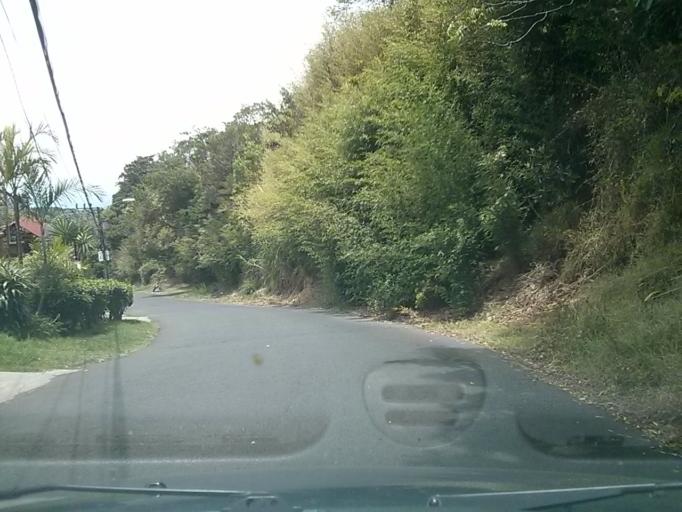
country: CR
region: Heredia
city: Santo Domingo
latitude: 10.0760
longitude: -84.1070
